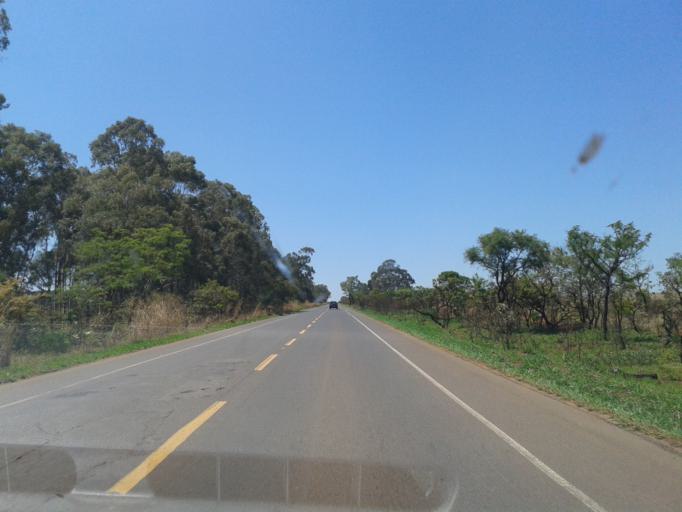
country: BR
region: Minas Gerais
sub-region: Araxa
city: Araxa
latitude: -19.3949
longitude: -47.3293
